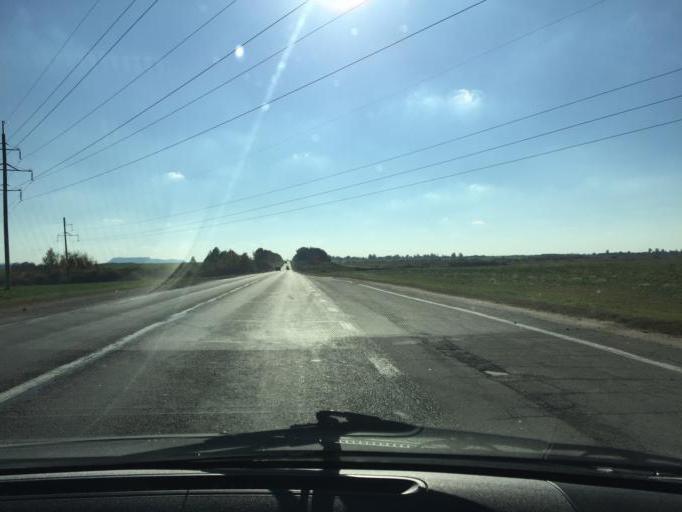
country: BY
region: Minsk
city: Slutsk
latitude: 52.9785
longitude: 27.5033
